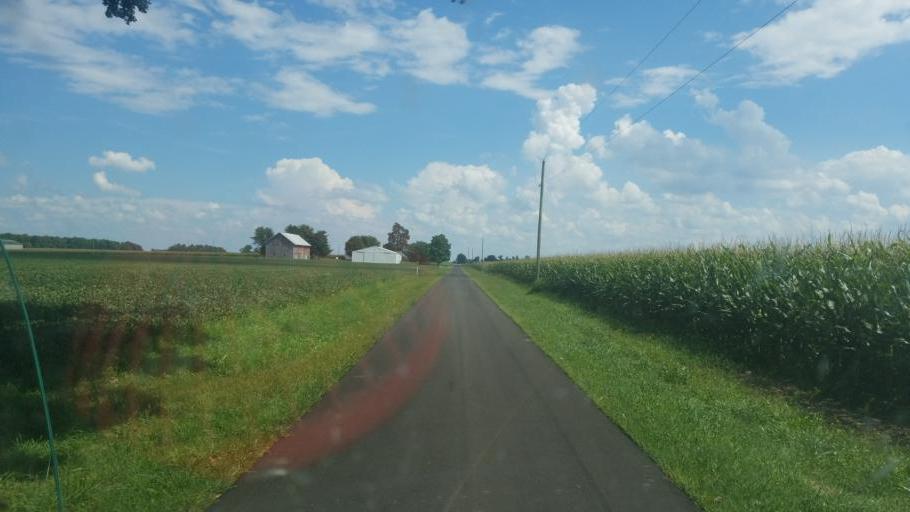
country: US
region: Ohio
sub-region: Hardin County
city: Forest
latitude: 40.8470
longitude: -83.4426
